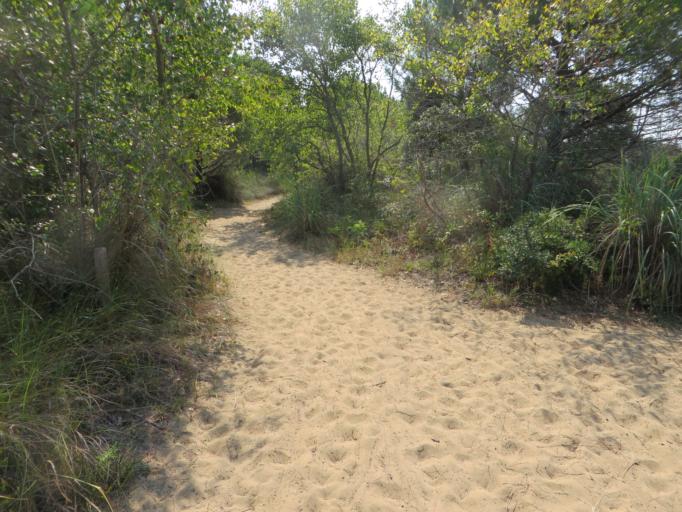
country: IT
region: Veneto
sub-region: Provincia di Venezia
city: Crepaldo
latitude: 45.5338
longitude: 12.7377
